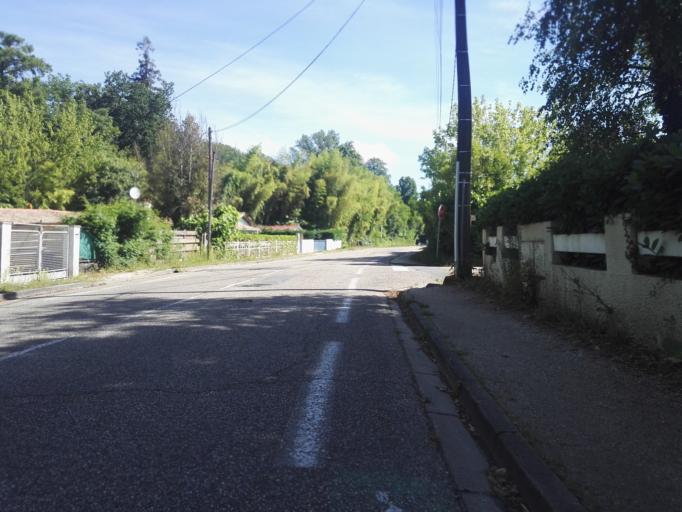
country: FR
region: Aquitaine
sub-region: Departement de la Gironde
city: Leognan
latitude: 44.7346
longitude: -0.5917
